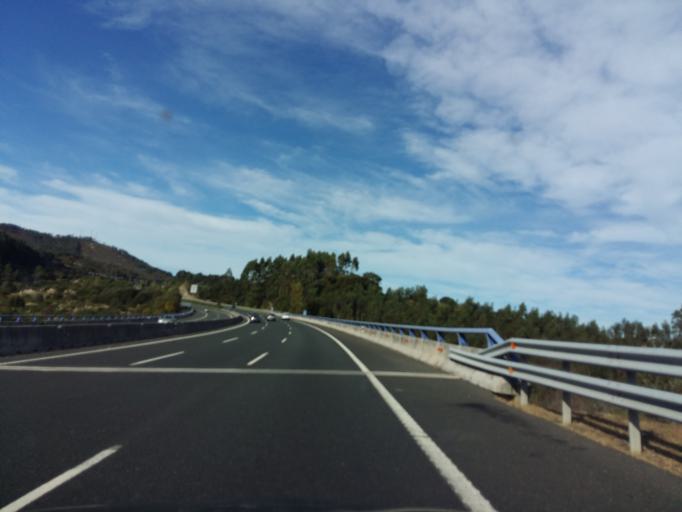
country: ES
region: Cantabria
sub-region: Provincia de Cantabria
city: Comillas
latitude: 43.3422
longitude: -4.3412
